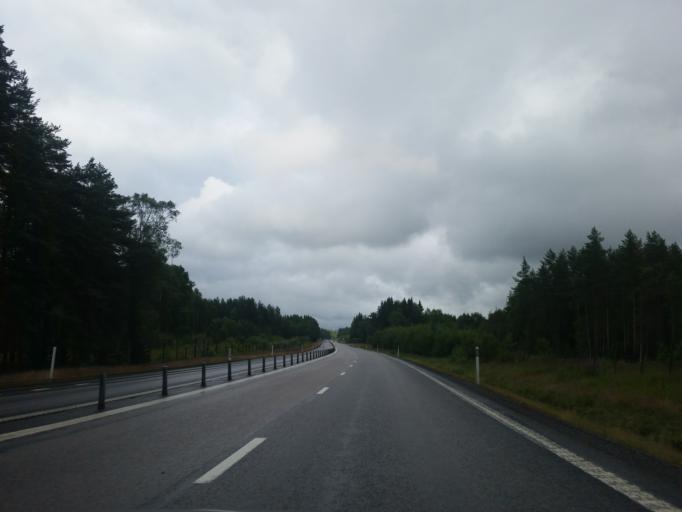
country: SE
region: Vaesterbotten
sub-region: Umea Kommun
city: Saevar
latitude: 63.9057
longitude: 20.5816
